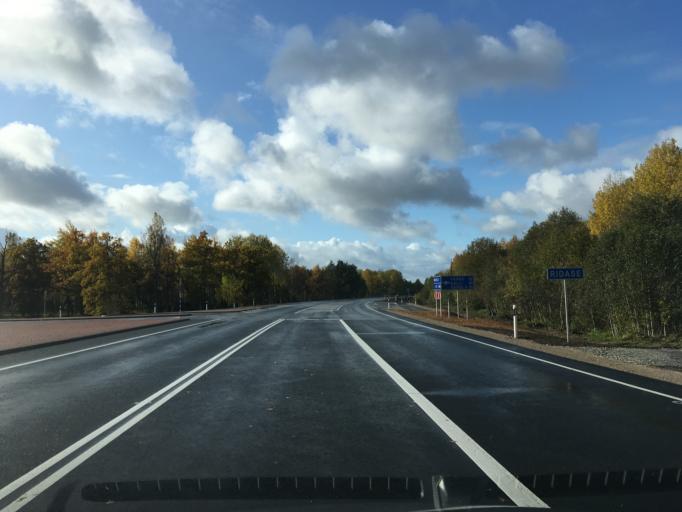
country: EE
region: Laeaene
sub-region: Lihula vald
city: Lihula
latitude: 58.6287
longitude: 23.6831
